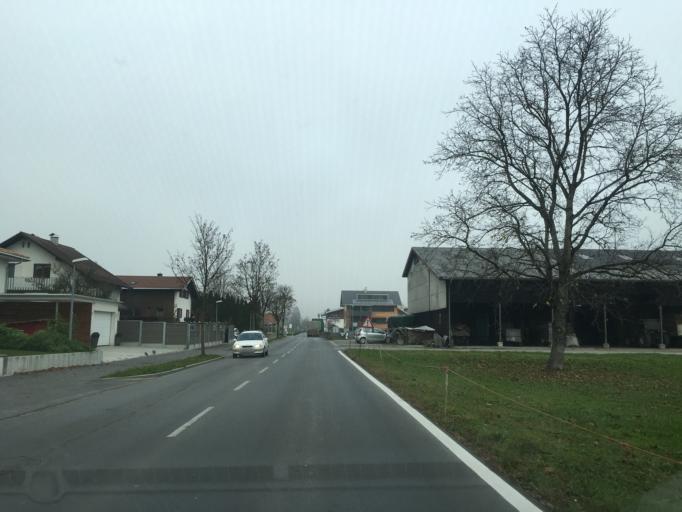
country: AT
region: Vorarlberg
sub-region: Politischer Bezirk Dornbirn
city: Lustenau
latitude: 47.4238
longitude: 9.6737
